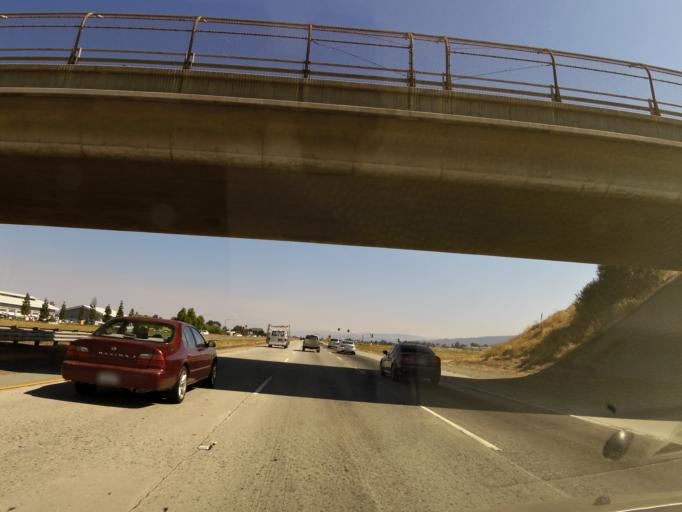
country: US
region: California
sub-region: Santa Clara County
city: San Martin
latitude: 37.0891
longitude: -121.5997
